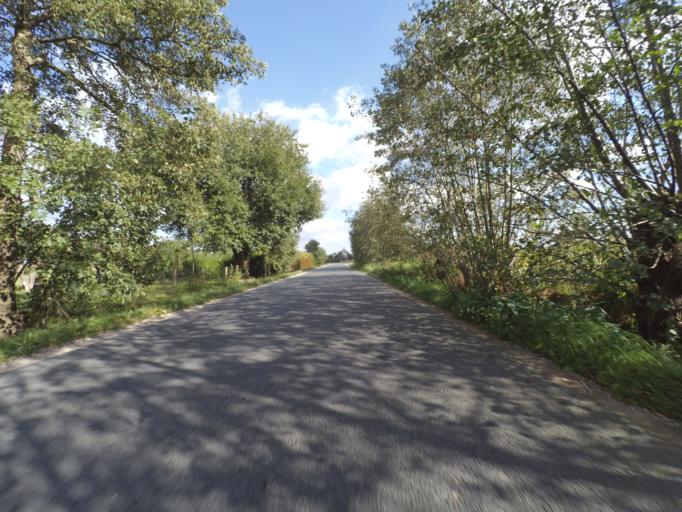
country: NL
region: Gelderland
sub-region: Gemeente Ede
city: Ederveen
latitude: 52.0578
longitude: 5.5781
